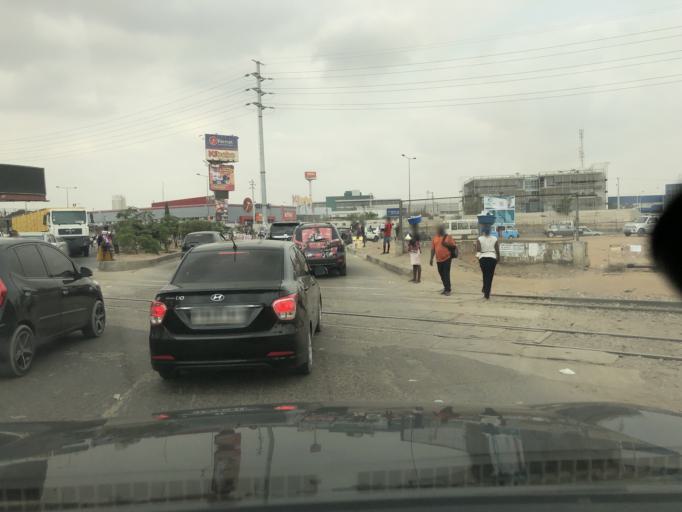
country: AO
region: Luanda
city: Luanda
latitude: -8.8481
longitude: 13.2848
